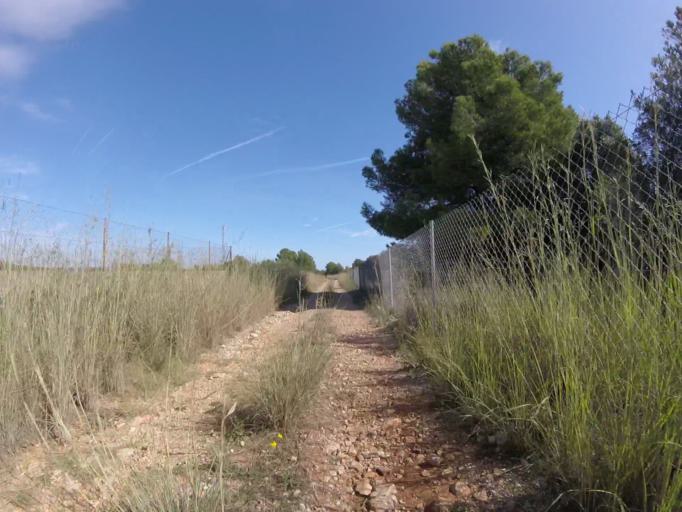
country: ES
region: Valencia
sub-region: Provincia de Castello
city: Peniscola
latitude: 40.3930
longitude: 0.3628
